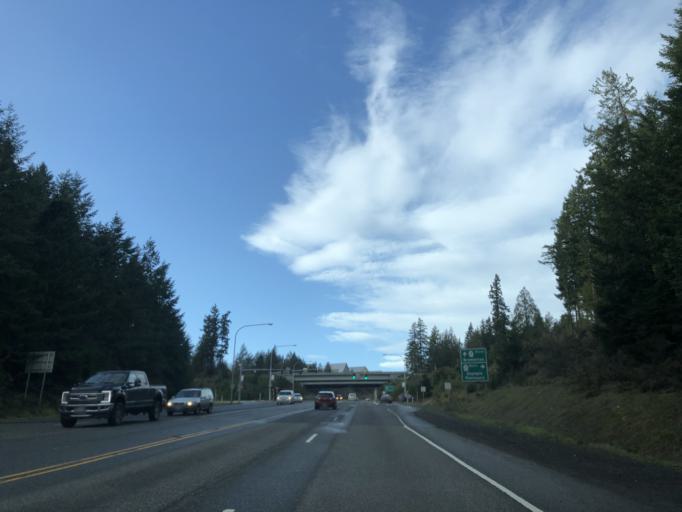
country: US
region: Washington
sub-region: Kitsap County
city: Poulsbo
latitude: 47.7576
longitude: -122.6534
